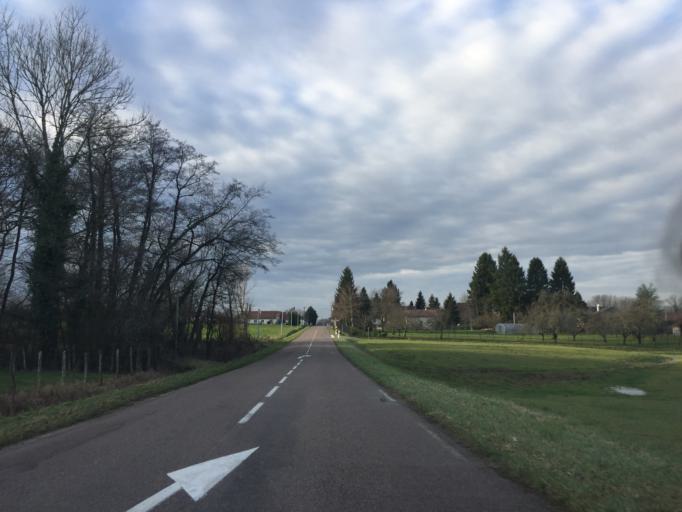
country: FR
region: Franche-Comte
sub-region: Departement du Jura
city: Mont-sous-Vaudrey
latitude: 46.9302
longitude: 5.6810
